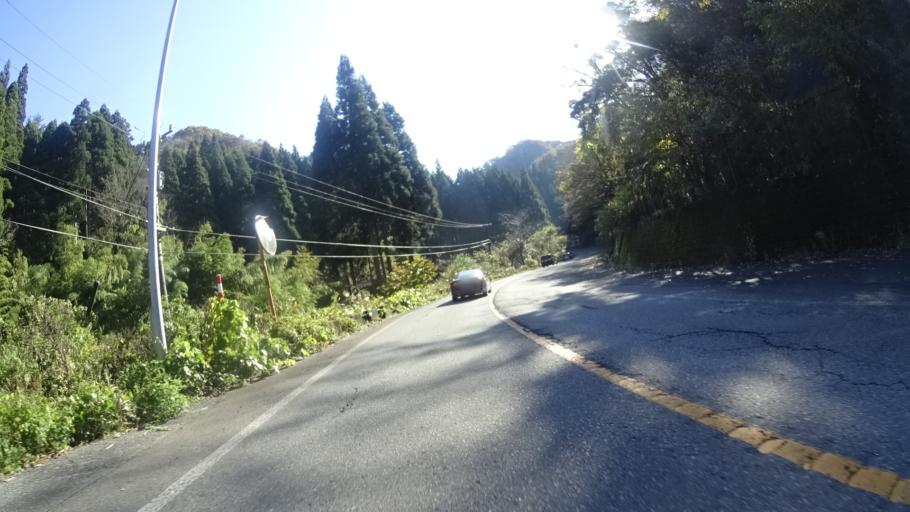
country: JP
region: Ishikawa
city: Tsurugi-asahimachi
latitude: 36.3734
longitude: 136.5761
